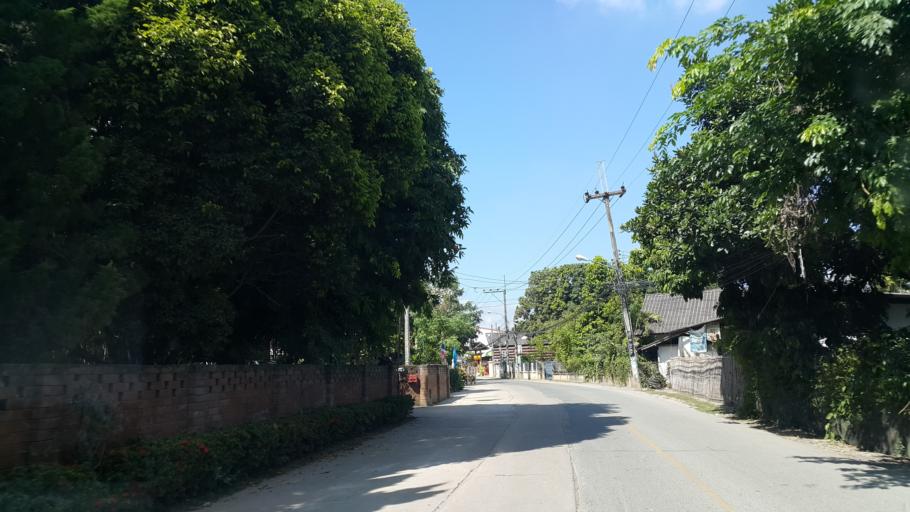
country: TH
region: Chiang Mai
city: San Sai
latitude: 18.8353
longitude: 99.0195
